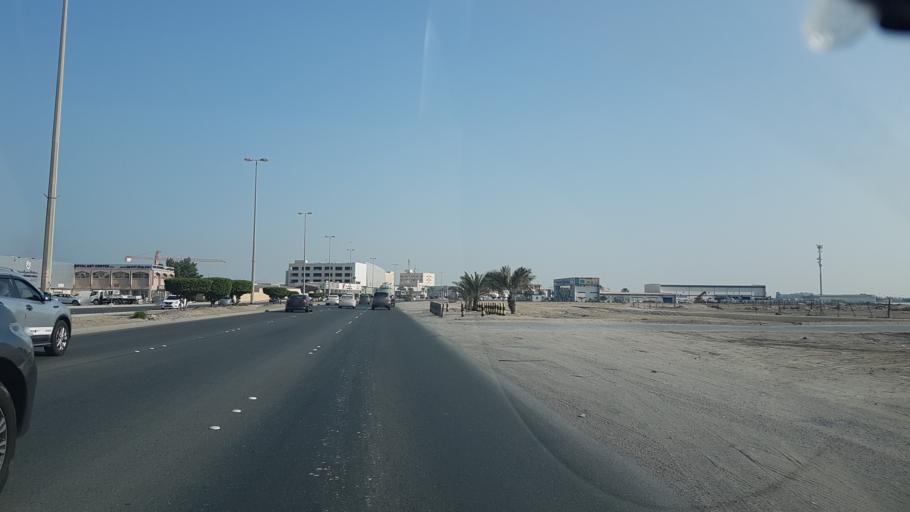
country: BH
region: Northern
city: Sitrah
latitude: 26.1538
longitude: 50.6133
